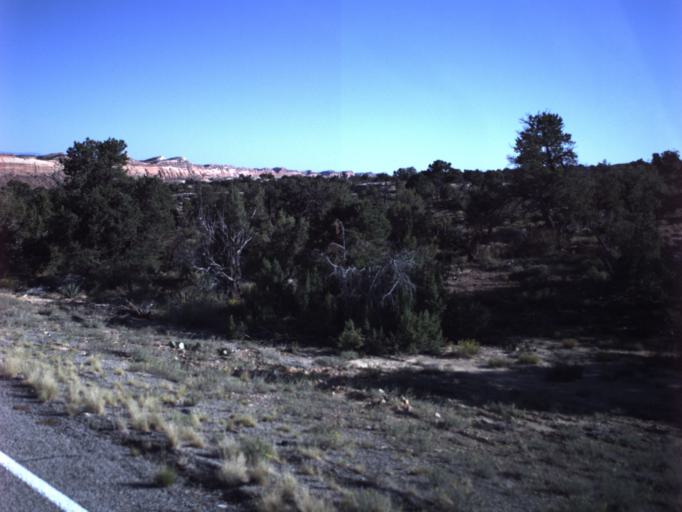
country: US
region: Utah
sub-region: San Juan County
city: Blanding
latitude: 37.5226
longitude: -109.6718
